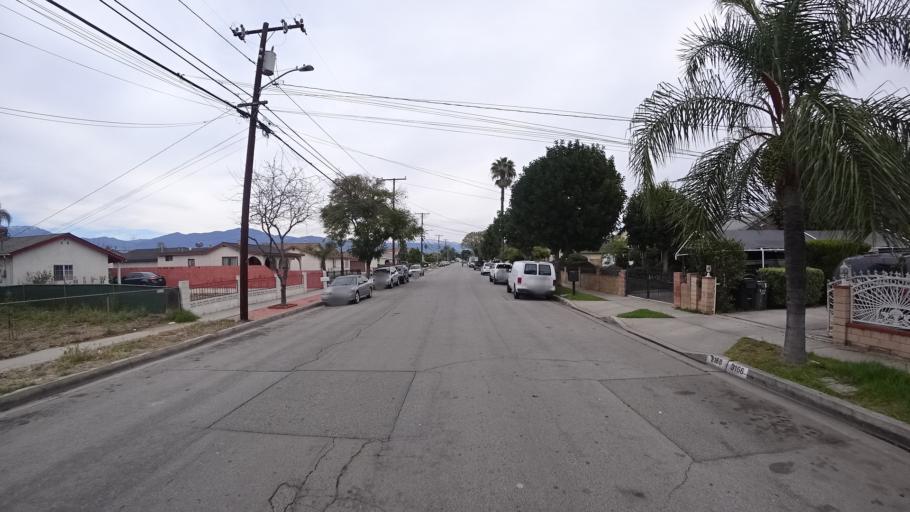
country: US
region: California
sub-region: Los Angeles County
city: West Puente Valley
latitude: 34.0689
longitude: -117.9907
